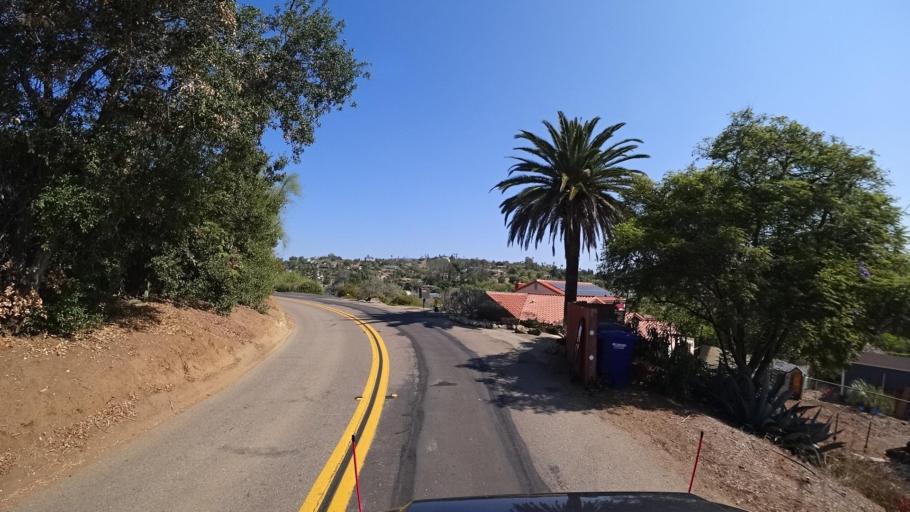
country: US
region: California
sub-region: San Diego County
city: Vista
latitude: 33.1790
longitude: -117.2124
